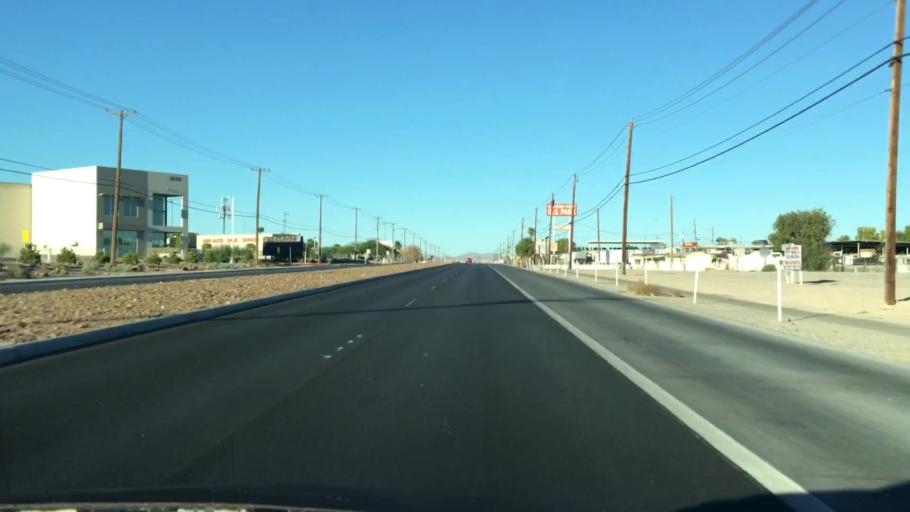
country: US
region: Nevada
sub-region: Clark County
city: Sunrise Manor
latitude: 36.2218
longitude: -115.0862
